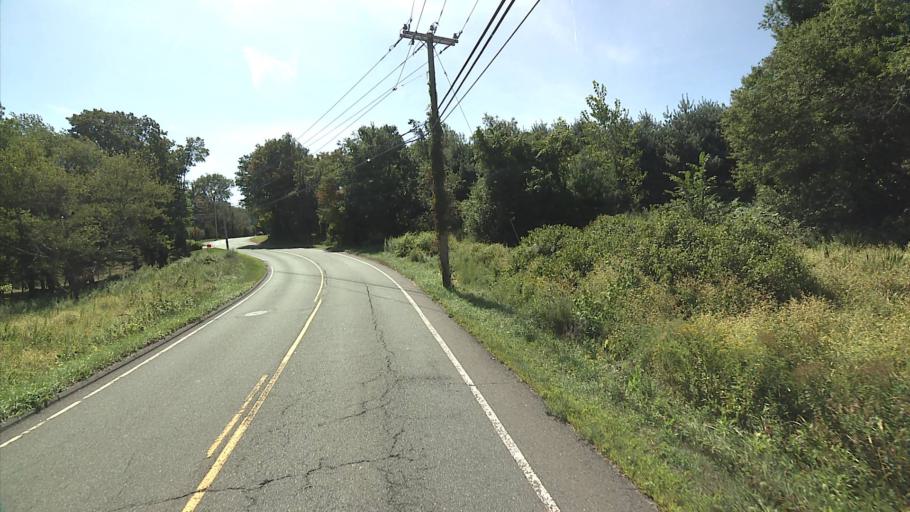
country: US
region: Connecticut
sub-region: New Haven County
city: Middlebury
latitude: 41.5118
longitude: -73.1433
